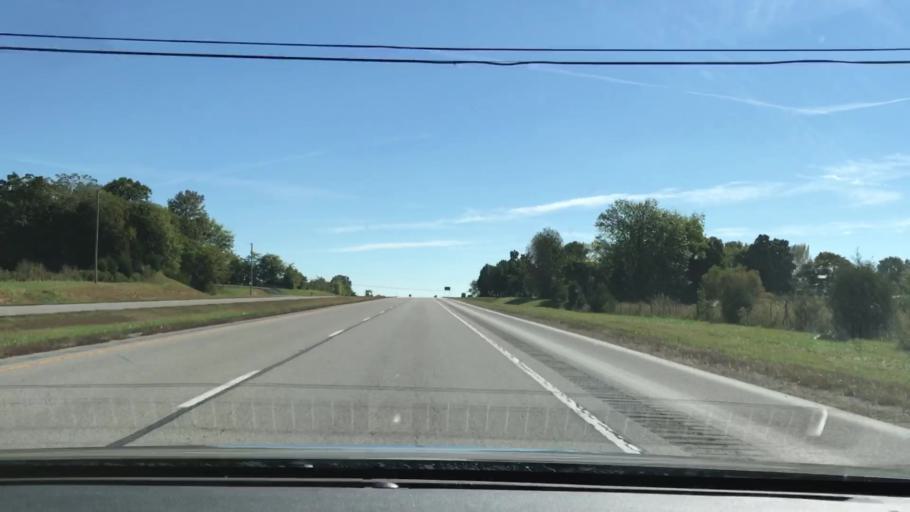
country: US
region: Kentucky
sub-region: Todd County
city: Elkton
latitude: 36.8240
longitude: -87.2063
